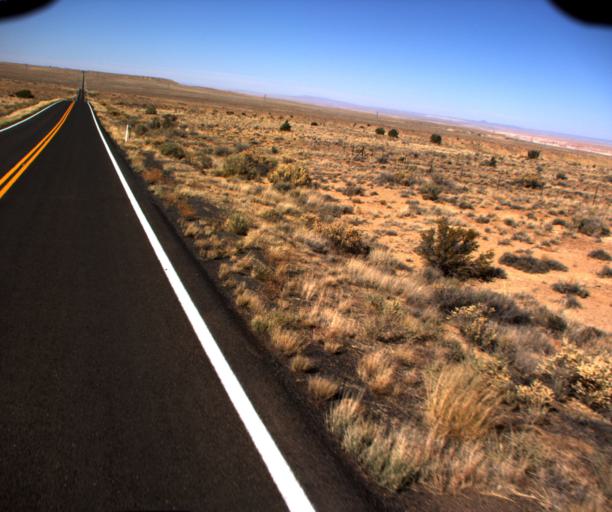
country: US
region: Arizona
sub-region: Coconino County
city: Tuba City
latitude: 35.9323
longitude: -110.8947
